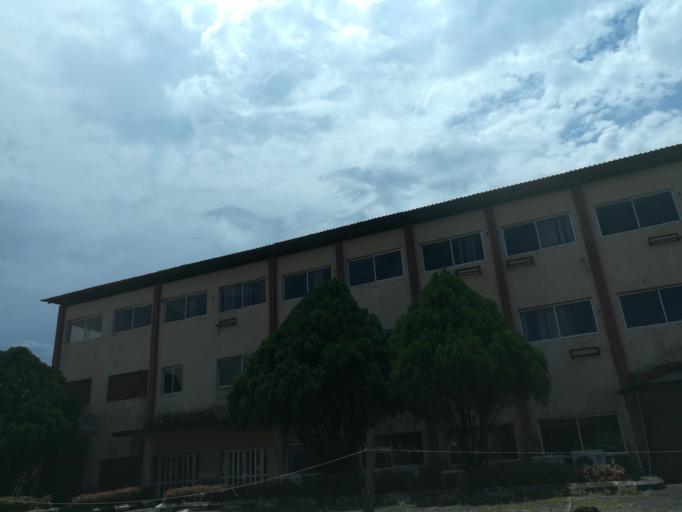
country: NG
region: Lagos
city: Agege
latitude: 6.6043
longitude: 3.3272
